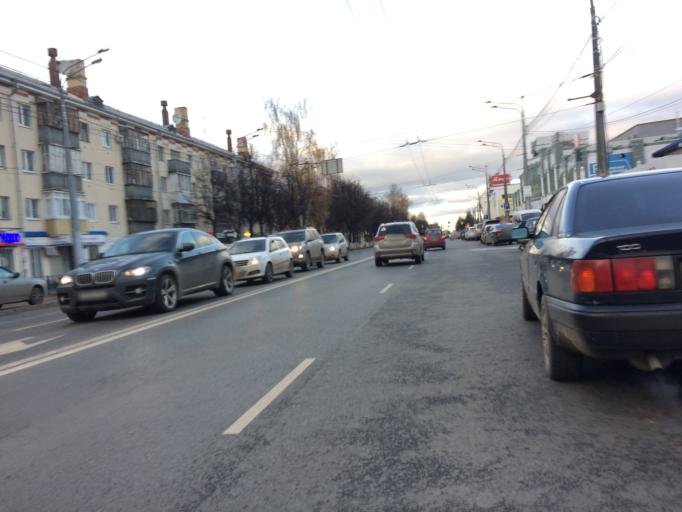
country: RU
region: Mariy-El
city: Yoshkar-Ola
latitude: 56.6325
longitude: 47.8834
